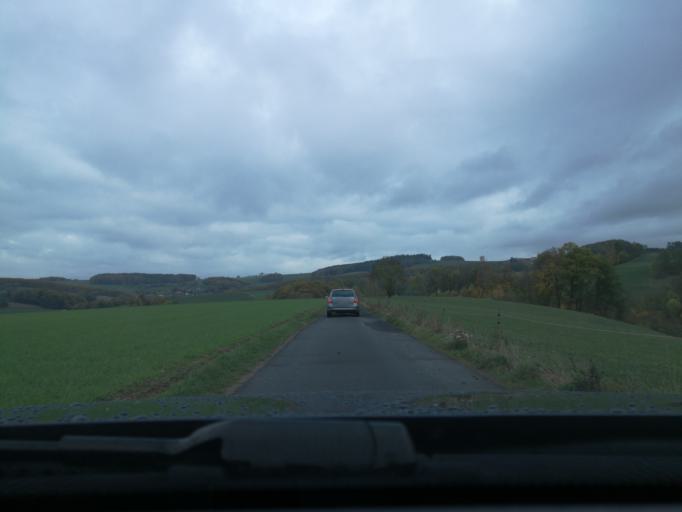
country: DE
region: Hesse
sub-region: Regierungsbezirk Kassel
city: Poppenhausen
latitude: 50.4868
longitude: 9.8563
